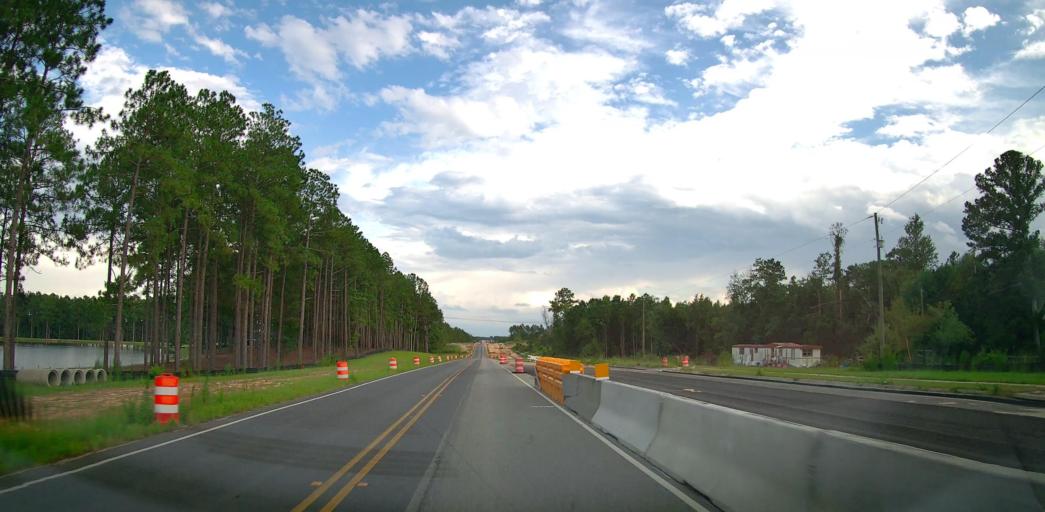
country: US
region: Georgia
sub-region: Dodge County
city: Eastman
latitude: 32.2751
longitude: -83.2481
